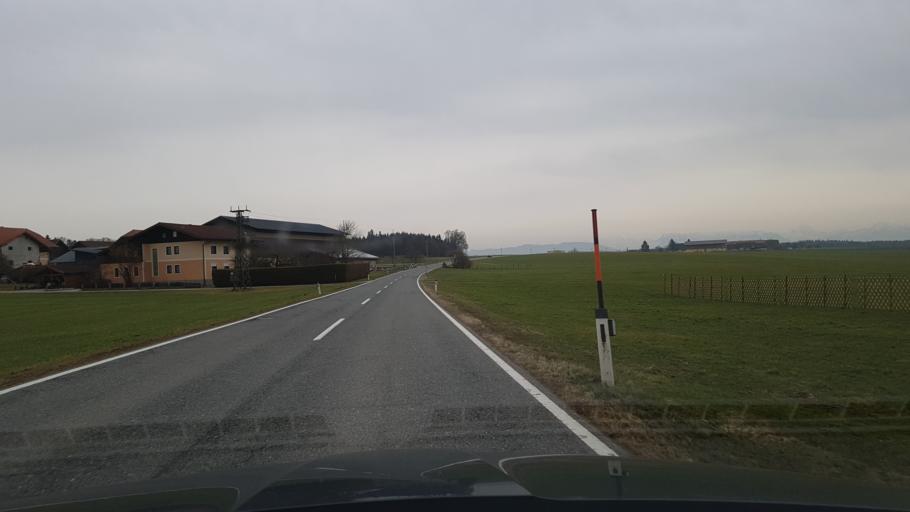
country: AT
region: Salzburg
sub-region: Politischer Bezirk Salzburg-Umgebung
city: Lamprechtshausen
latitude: 48.0272
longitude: 12.9572
